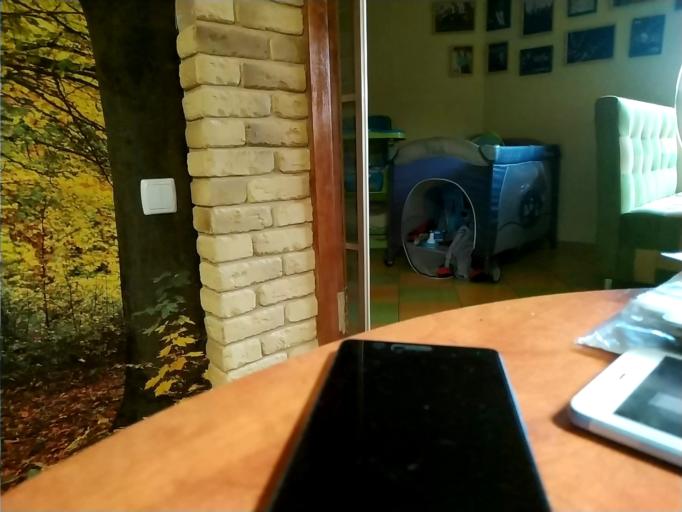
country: RU
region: Kaluga
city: Khvastovichi
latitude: 53.6683
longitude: 35.4434
